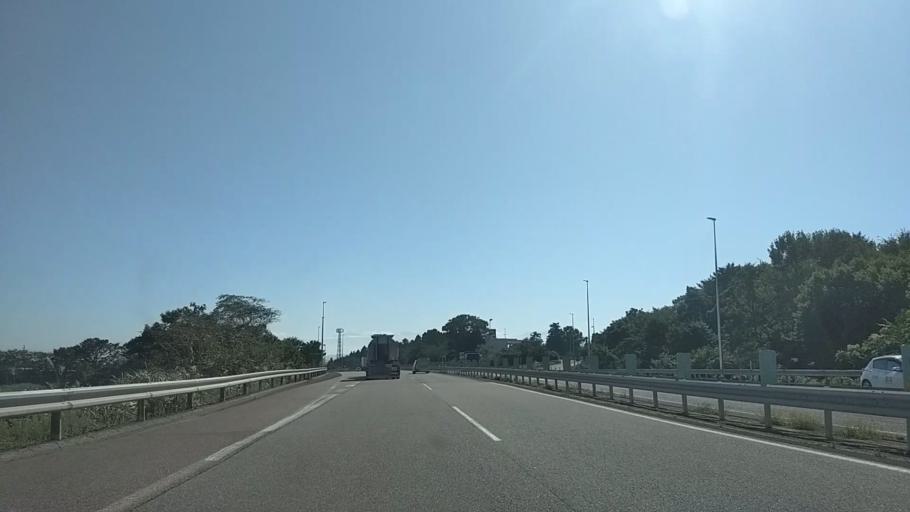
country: JP
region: Toyama
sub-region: Oyabe Shi
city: Oyabe
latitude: 36.6269
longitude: 136.8696
